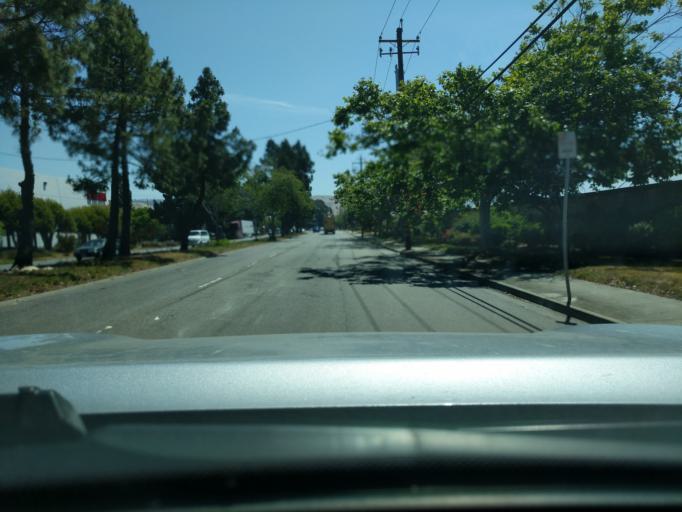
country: US
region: California
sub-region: Alameda County
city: Union City
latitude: 37.6177
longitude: -122.0666
